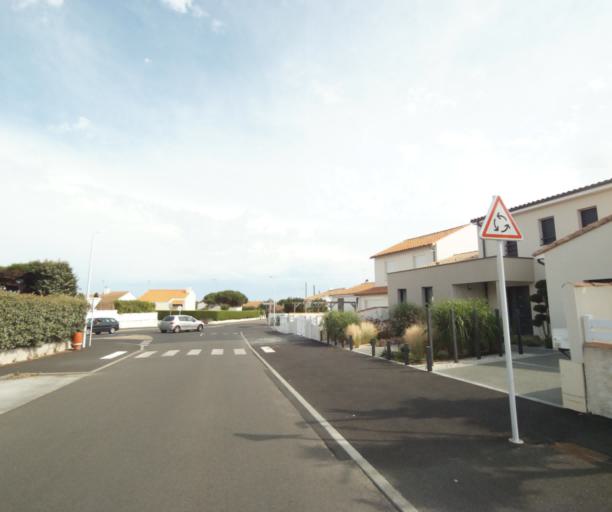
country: FR
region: Pays de la Loire
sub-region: Departement de la Vendee
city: Chateau-d'Olonne
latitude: 46.4816
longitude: -1.7489
